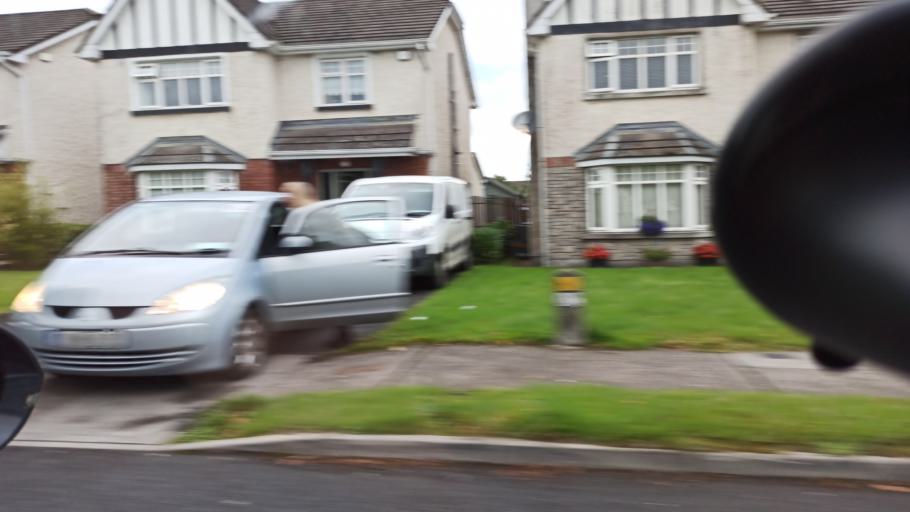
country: IE
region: Munster
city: Thurles
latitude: 52.6669
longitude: -7.8132
